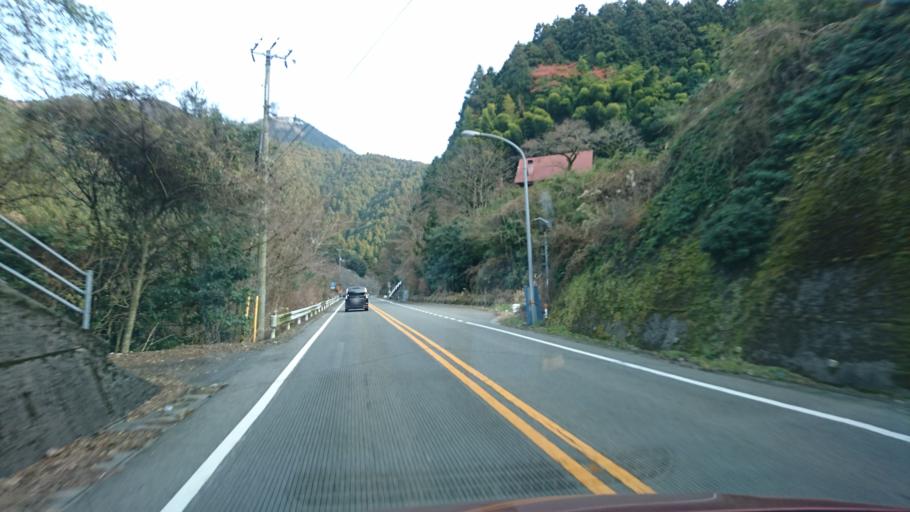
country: JP
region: Ehime
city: Hojo
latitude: 33.9562
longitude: 132.9093
